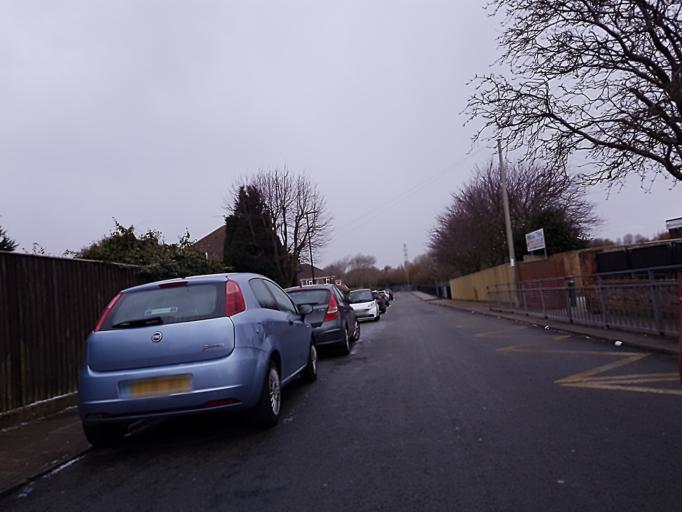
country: GB
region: England
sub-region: North East Lincolnshire
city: Grimbsy
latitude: 53.5629
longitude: -0.1162
